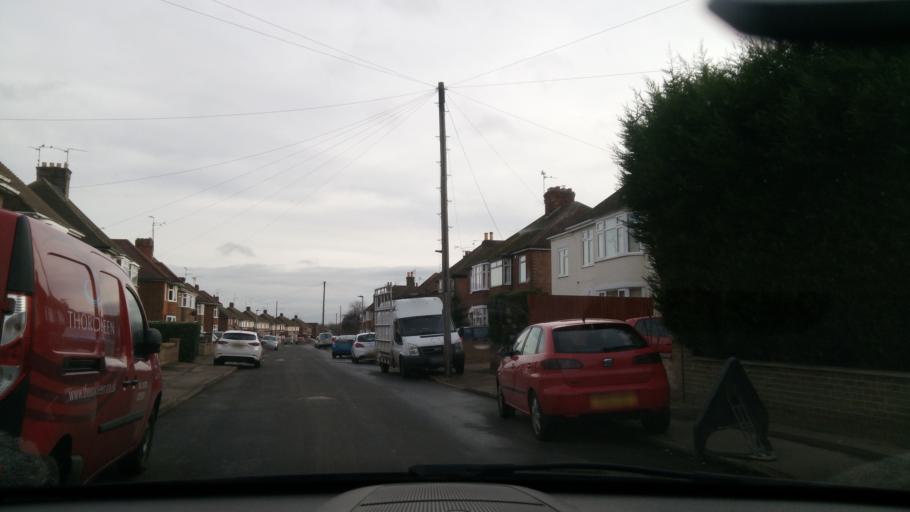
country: GB
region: England
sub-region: Peterborough
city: Peterborough
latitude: 52.5871
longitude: -0.2235
